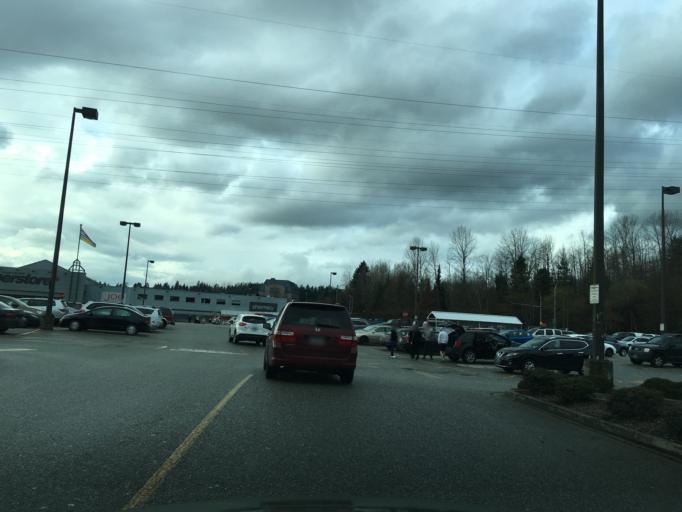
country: CA
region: British Columbia
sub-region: Fraser Valley Regional District
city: North Vancouver
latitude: 49.3111
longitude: -123.0223
